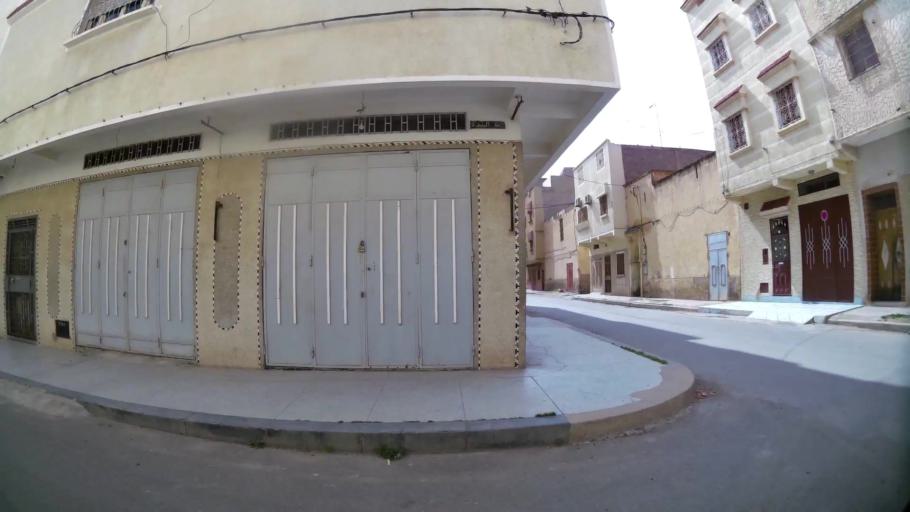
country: MA
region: Oriental
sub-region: Oujda-Angad
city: Oujda
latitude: 34.6872
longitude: -1.9089
